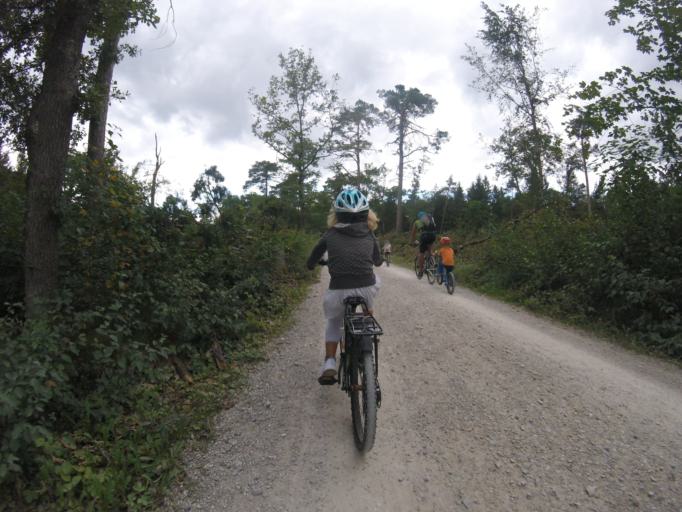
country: CH
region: Bern
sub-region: Bern-Mittelland District
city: Rubigen
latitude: 46.8839
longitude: 7.5335
